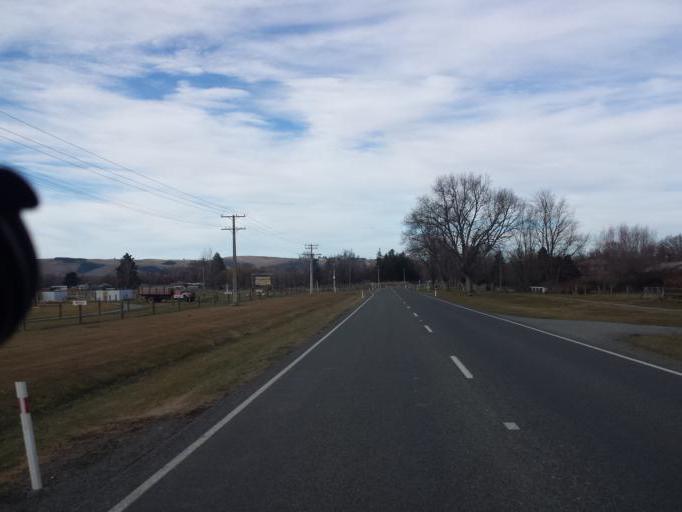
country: NZ
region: Canterbury
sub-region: Timaru District
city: Pleasant Point
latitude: -44.0886
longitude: 170.8168
